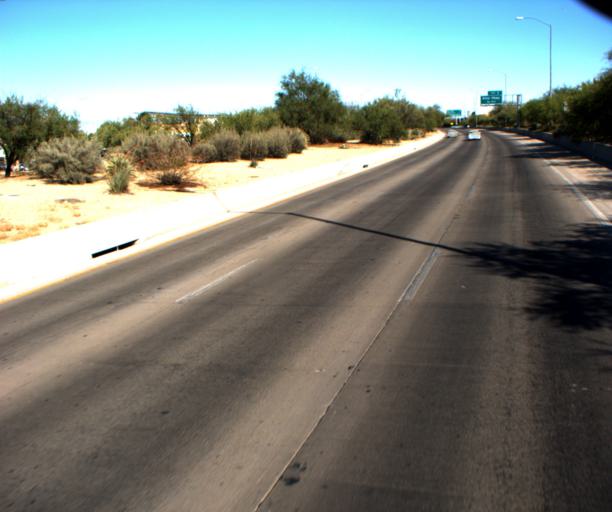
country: US
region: Arizona
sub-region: Pima County
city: South Tucson
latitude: 32.2180
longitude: -110.9596
